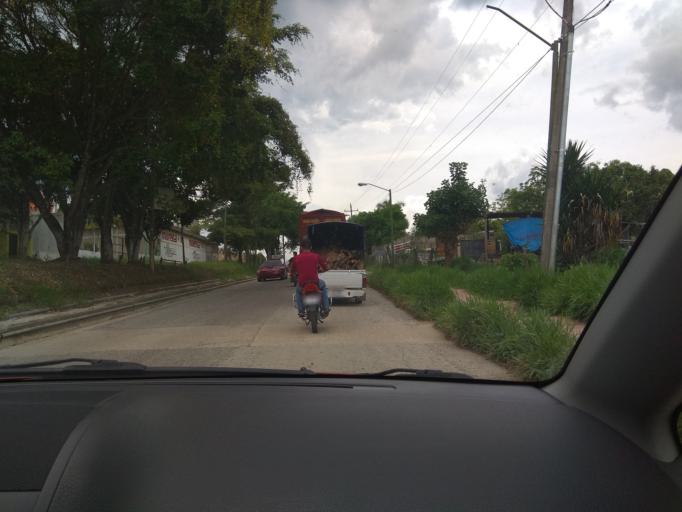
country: MX
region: Chiapas
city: Ocosingo
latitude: 16.8992
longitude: -92.0795
